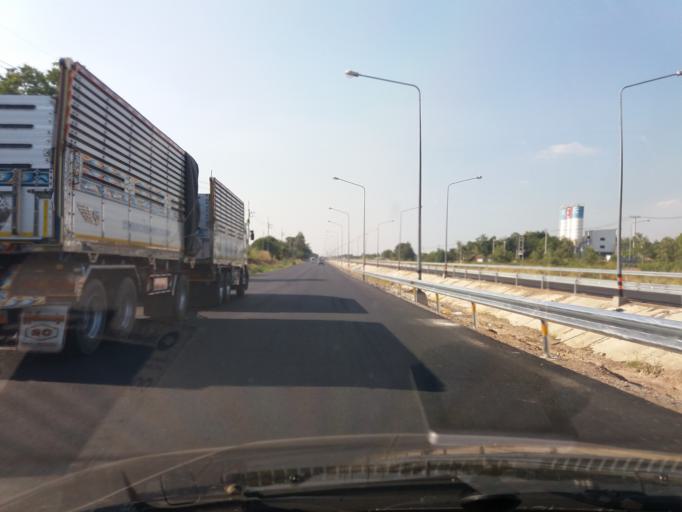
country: TH
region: Nakhon Sawan
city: Krok Phra
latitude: 15.6184
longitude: 100.1182
